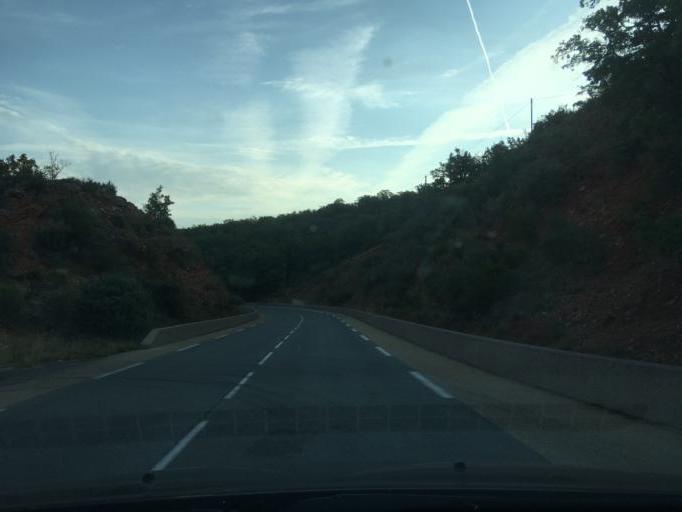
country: FR
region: Provence-Alpes-Cote d'Azur
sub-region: Departement du Var
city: Aups
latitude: 43.7434
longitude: 6.2227
